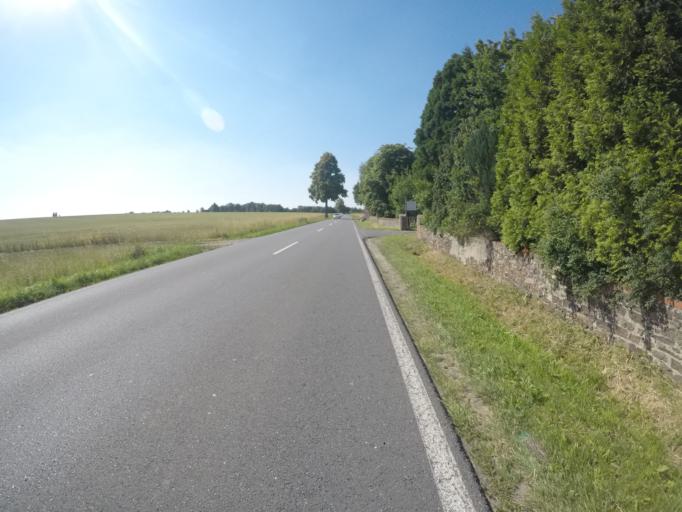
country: DE
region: North Rhine-Westphalia
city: Loehne
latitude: 52.1741
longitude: 8.7426
